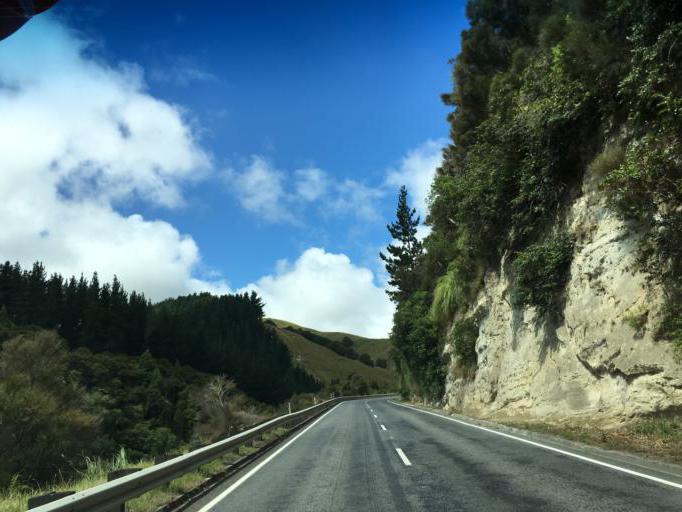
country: NZ
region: Hawke's Bay
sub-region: Napier City
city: Napier
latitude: -39.1299
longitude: 176.9995
